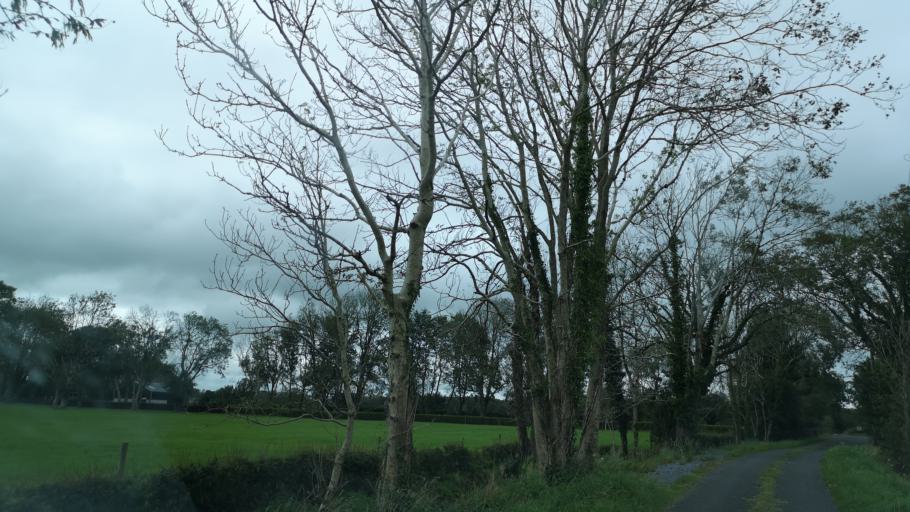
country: IE
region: Connaught
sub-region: County Galway
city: Athenry
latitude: 53.2991
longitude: -8.6676
